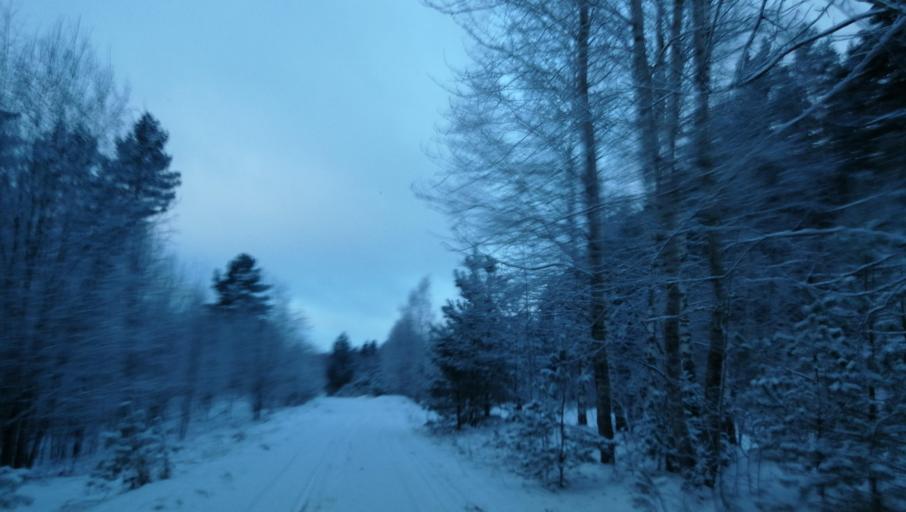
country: LV
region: Amatas Novads
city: Drabesi
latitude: 57.2075
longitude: 25.3177
